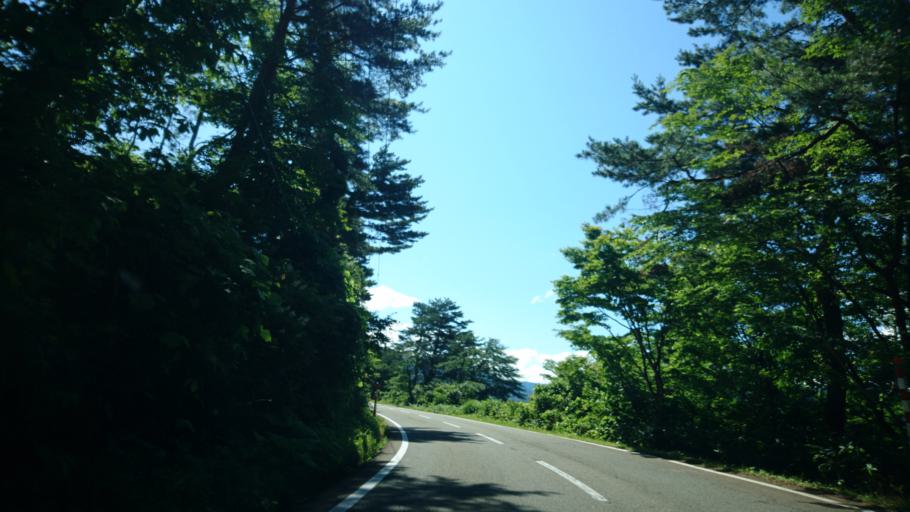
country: JP
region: Akita
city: Kakunodatemachi
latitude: 39.7501
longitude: 140.6589
